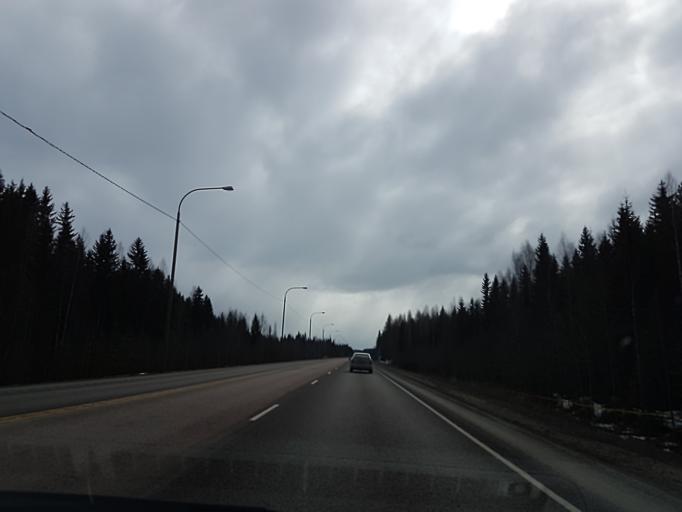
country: FI
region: Northern Savo
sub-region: Varkaus
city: Leppaevirta
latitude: 62.4332
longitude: 27.8114
